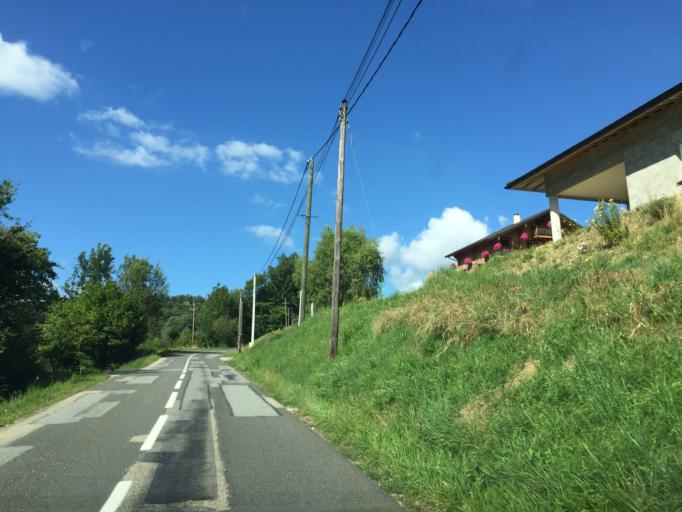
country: FR
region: Rhone-Alpes
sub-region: Departement de la Savoie
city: La Rochette
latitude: 45.4656
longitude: 6.1769
